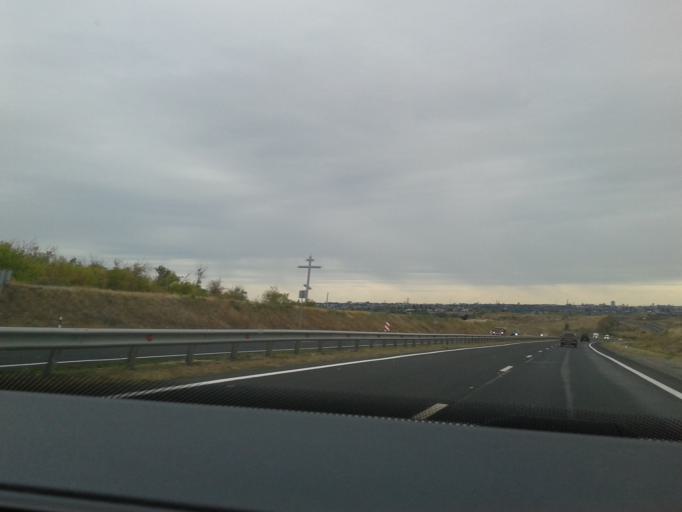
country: RU
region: Volgograd
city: Gorodishche
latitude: 48.8191
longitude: 44.4396
